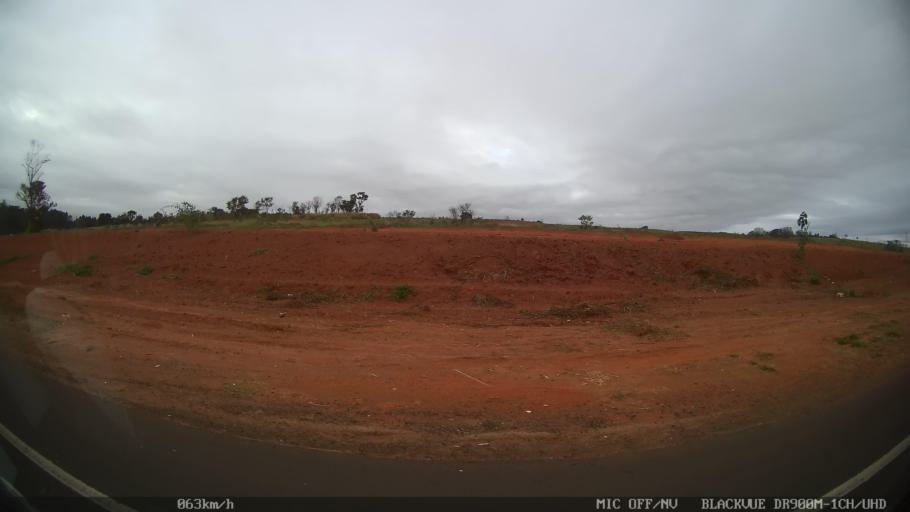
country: BR
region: Sao Paulo
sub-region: Sao Jose Do Rio Preto
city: Sao Jose do Rio Preto
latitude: -20.8216
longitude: -49.4366
